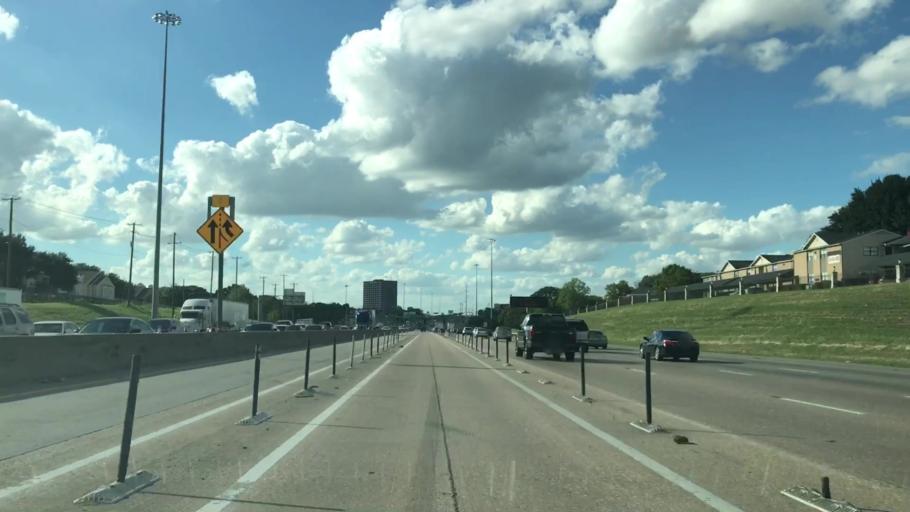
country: US
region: Texas
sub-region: Dallas County
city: Richardson
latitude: 32.9042
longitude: -96.7237
